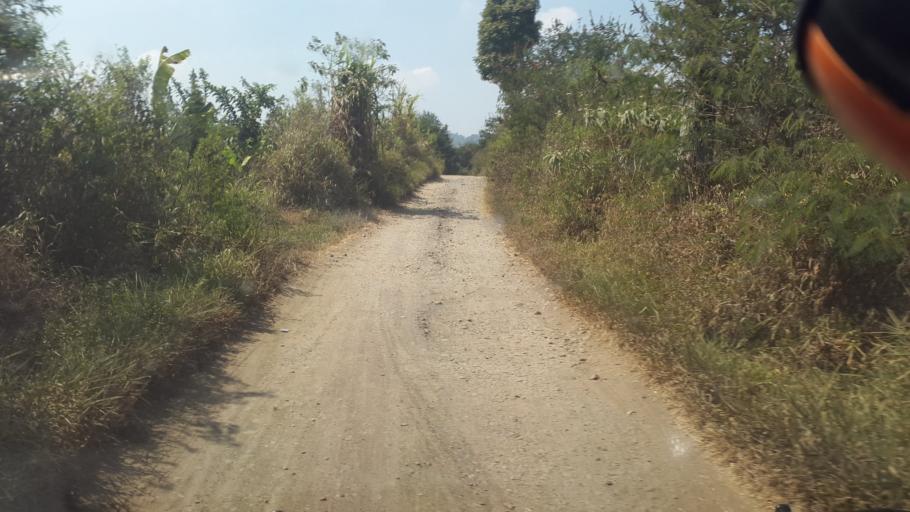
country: ID
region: West Java
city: Pasirreungit
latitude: -7.0100
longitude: 107.0233
